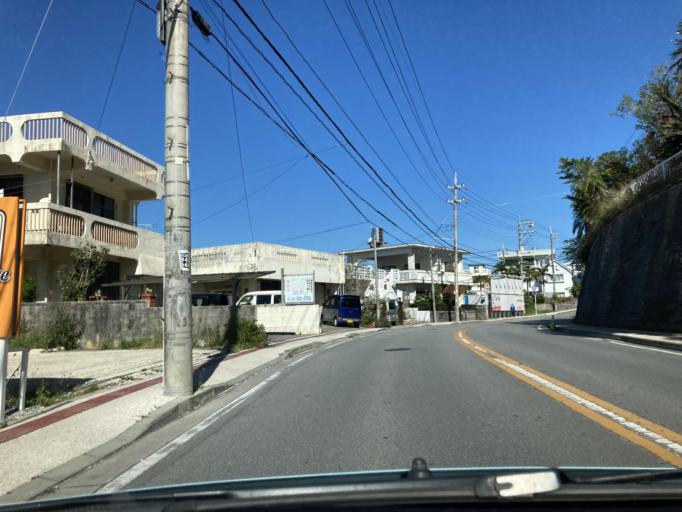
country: JP
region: Okinawa
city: Okinawa
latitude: 26.3268
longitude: 127.8019
